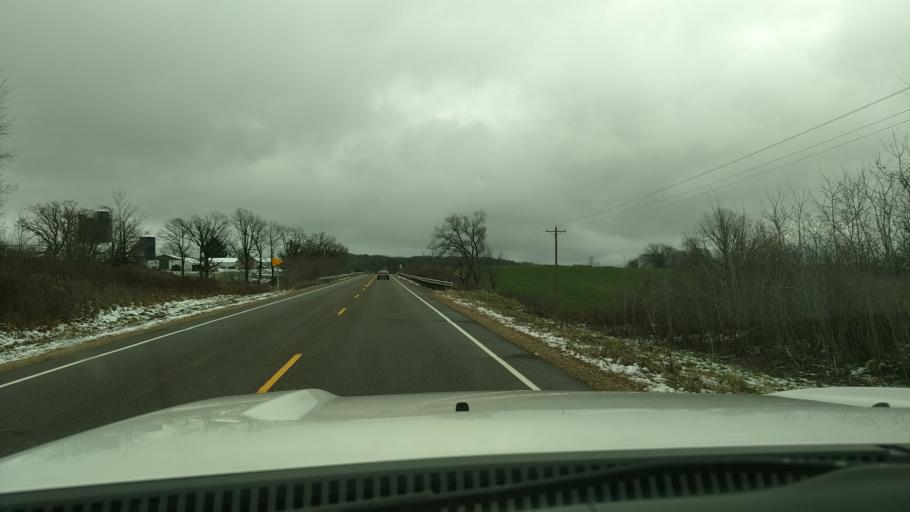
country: US
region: Wisconsin
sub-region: Dunn County
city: Boyceville
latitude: 45.1384
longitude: -91.9588
